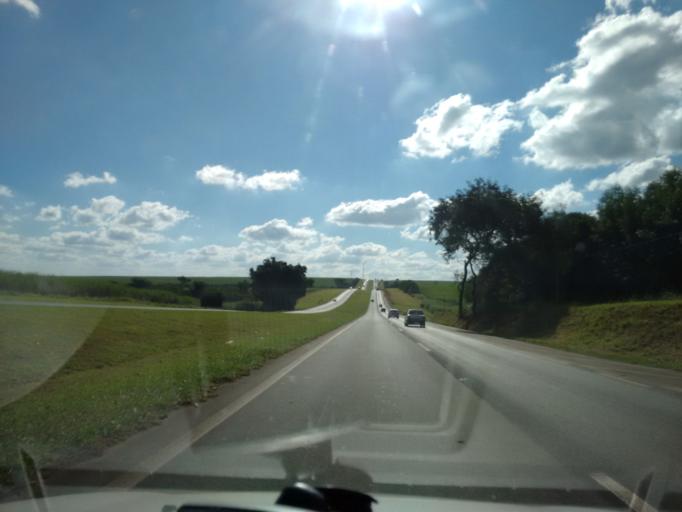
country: BR
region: Sao Paulo
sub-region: Araraquara
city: Araraquara
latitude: -21.8718
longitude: -48.1040
